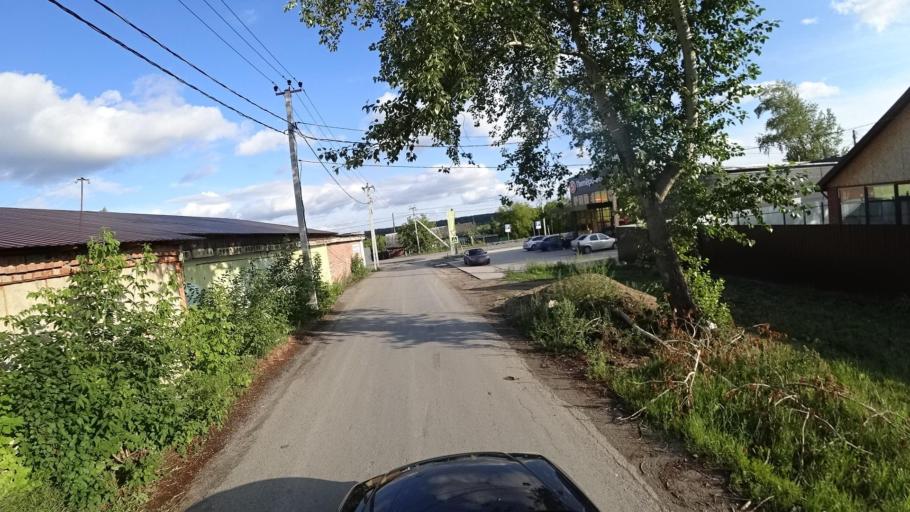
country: RU
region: Sverdlovsk
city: Obukhovskoye
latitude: 56.8470
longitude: 62.6546
